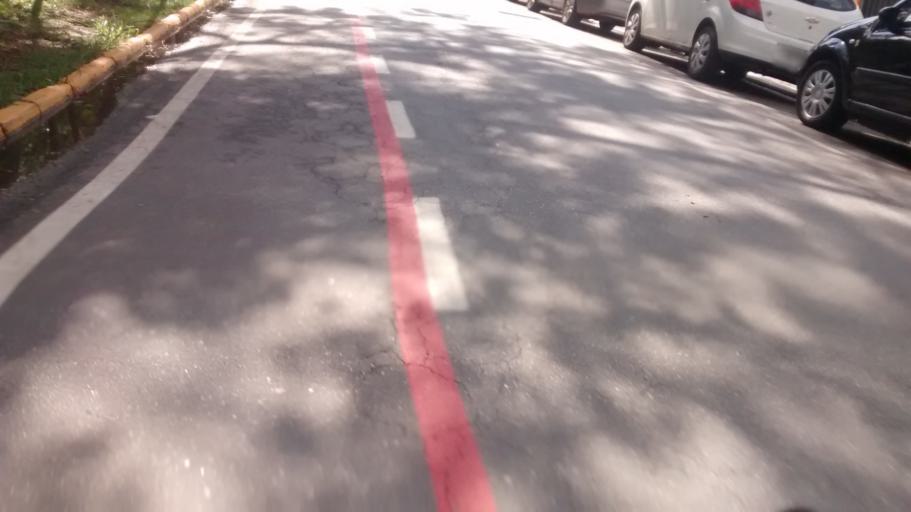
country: BR
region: Minas Gerais
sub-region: Itajuba
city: Itajuba
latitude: -22.4210
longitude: -45.4550
